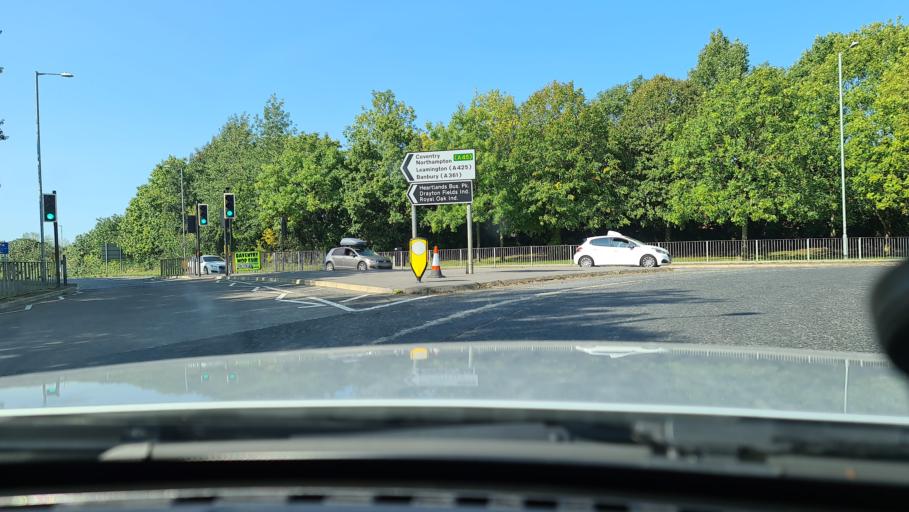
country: GB
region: England
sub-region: Northamptonshire
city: Daventry
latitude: 52.2763
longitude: -1.1657
